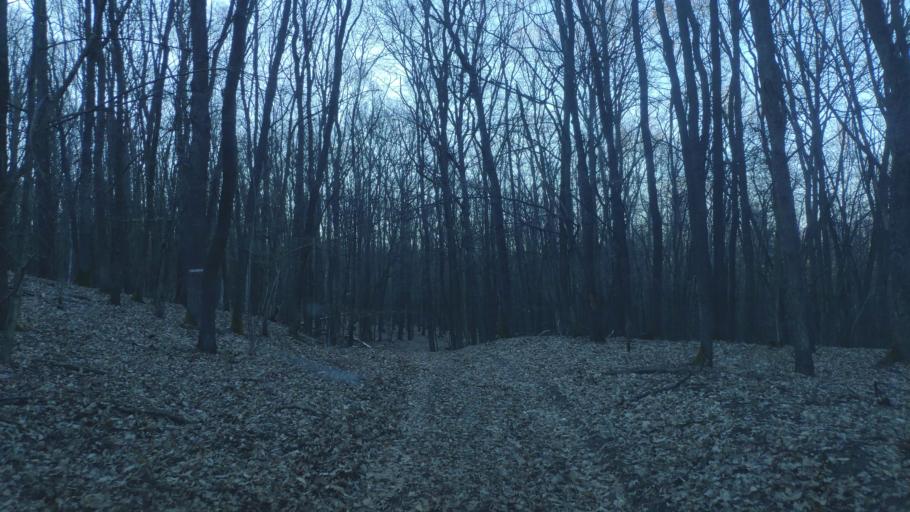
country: HU
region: Borsod-Abauj-Zemplen
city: Putnok
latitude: 48.5052
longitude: 20.3270
